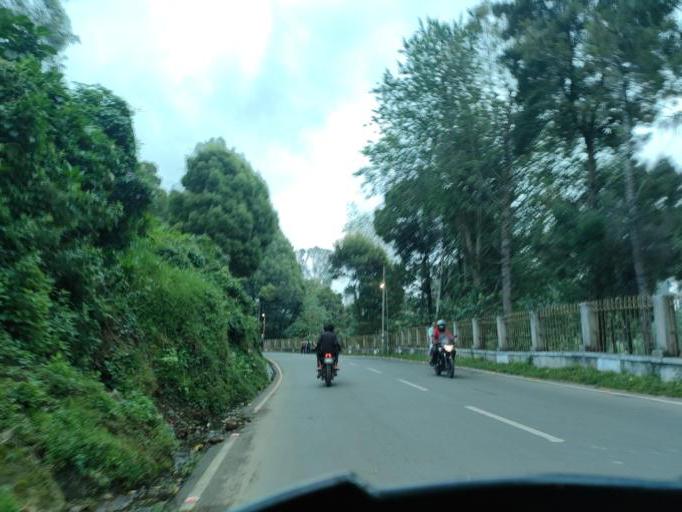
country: IN
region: Tamil Nadu
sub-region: Dindigul
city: Kodaikanal
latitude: 10.2377
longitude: 77.4934
